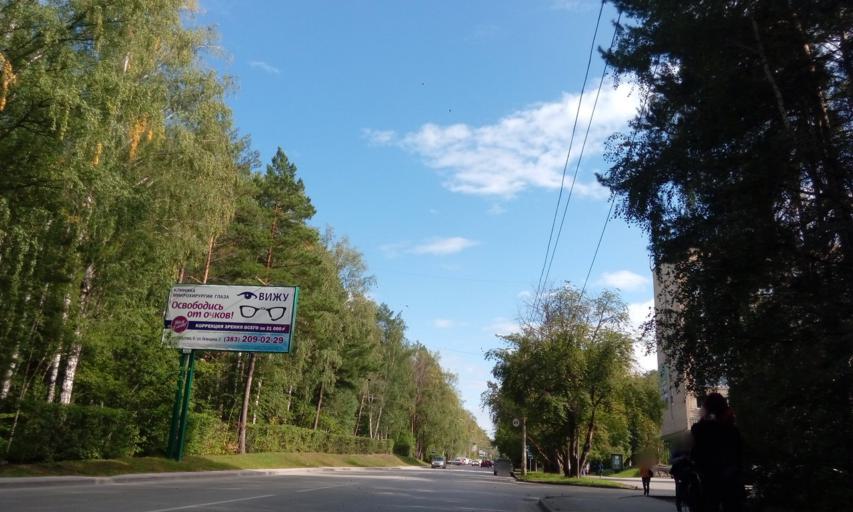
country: RU
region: Novosibirsk
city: Akademgorodok
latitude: 54.8422
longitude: 83.0926
